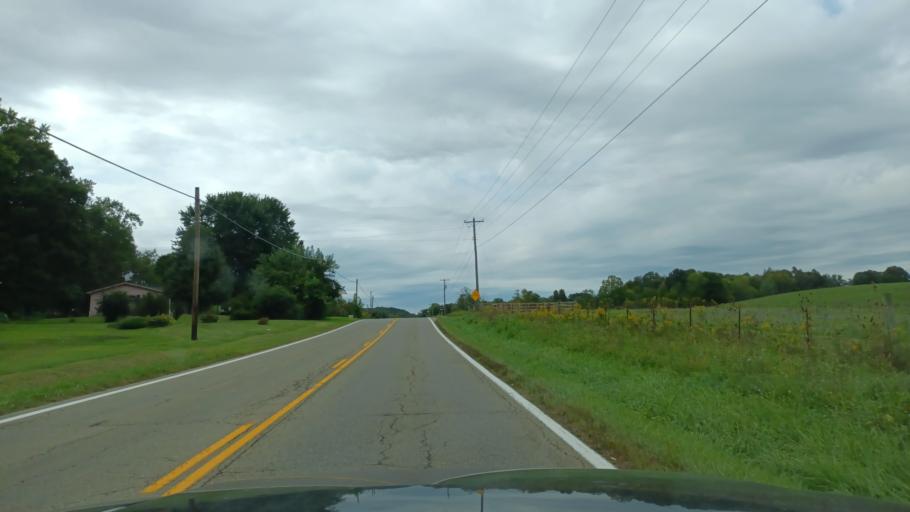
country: US
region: Ohio
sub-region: Vinton County
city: McArthur
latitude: 39.2583
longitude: -82.5015
